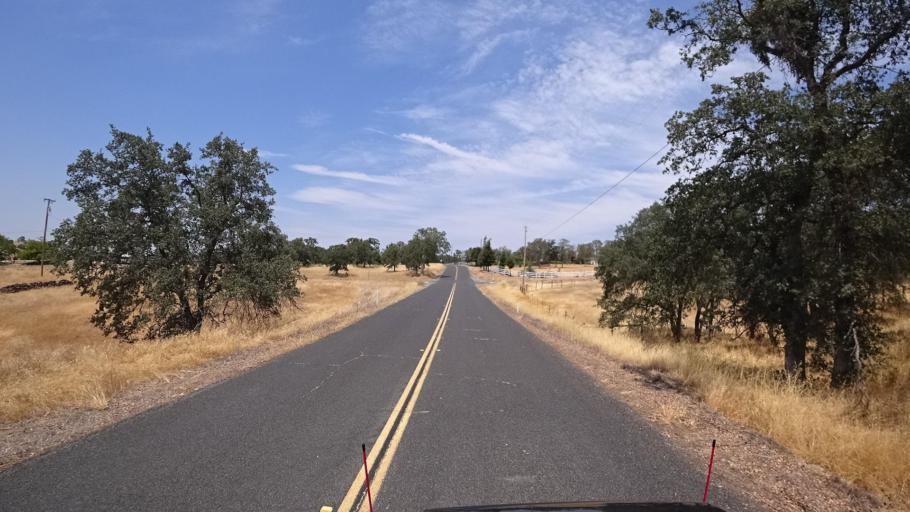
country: US
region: California
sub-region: Tuolumne County
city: Jamestown
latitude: 37.6383
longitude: -120.3247
